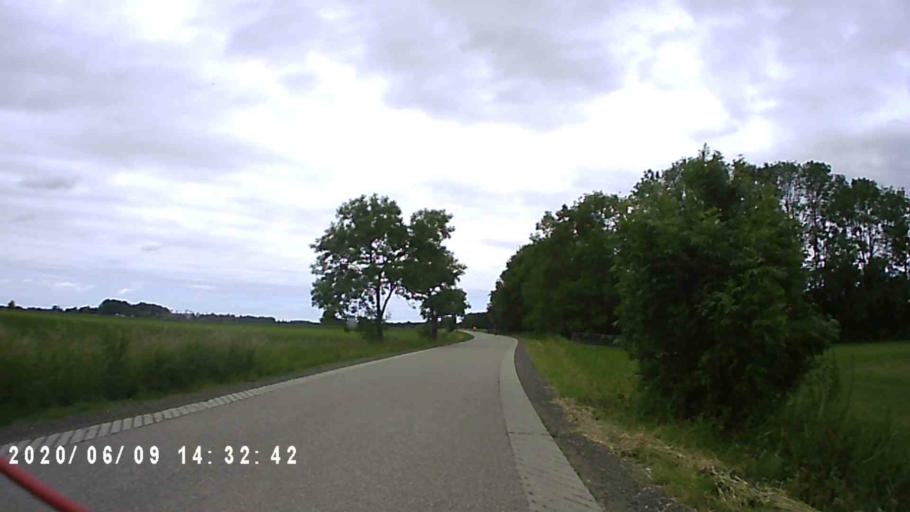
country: NL
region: Groningen
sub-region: Gemeente Bedum
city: Bedum
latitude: 53.3200
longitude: 6.5916
